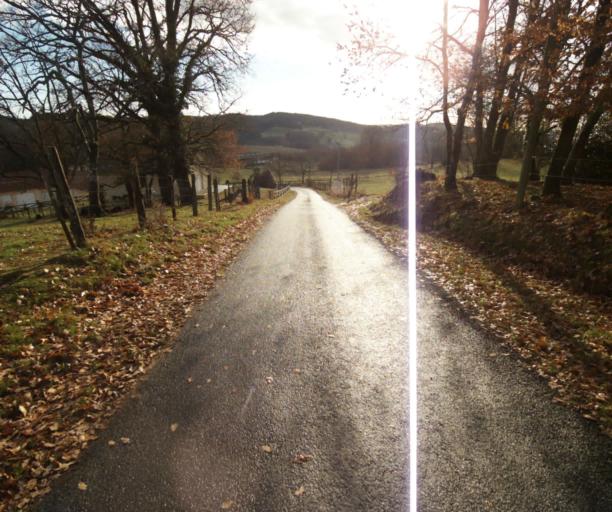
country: FR
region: Limousin
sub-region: Departement de la Correze
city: Saint-Mexant
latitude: 45.2493
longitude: 1.6355
